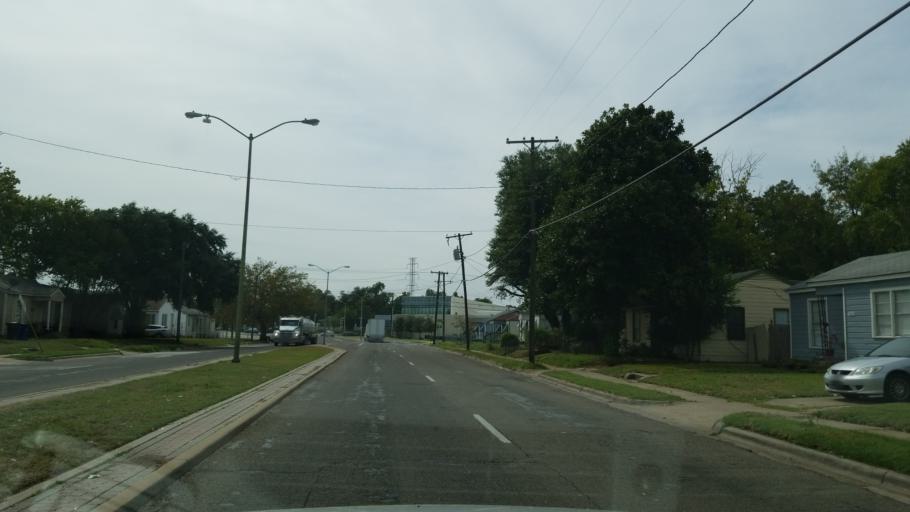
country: US
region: Texas
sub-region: Dallas County
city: Dallas
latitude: 32.7681
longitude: -96.7398
